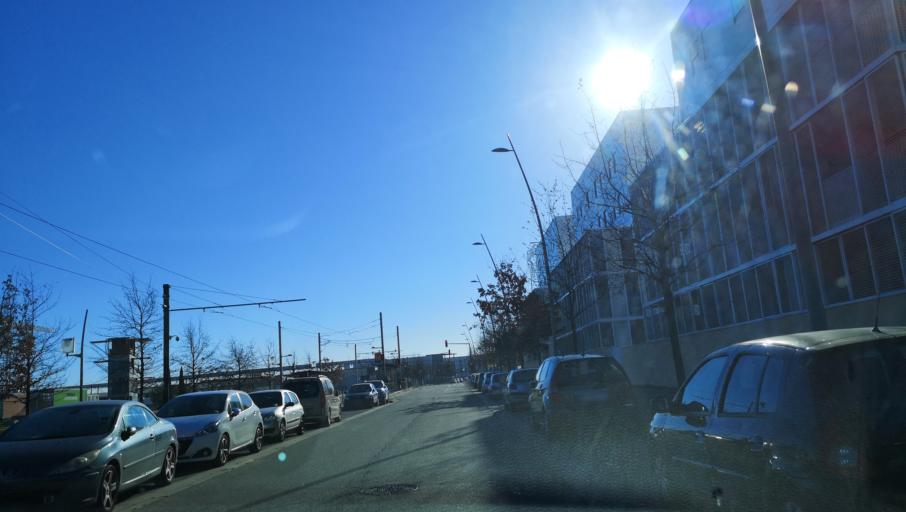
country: FR
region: Midi-Pyrenees
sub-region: Departement de la Haute-Garonne
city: Beauzelle
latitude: 43.6554
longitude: 1.3729
